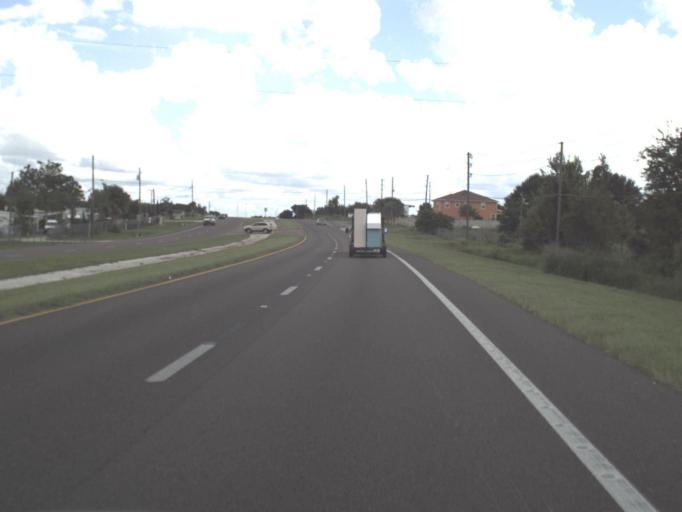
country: US
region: Florida
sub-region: Polk County
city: Haines City
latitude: 28.1066
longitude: -81.6600
